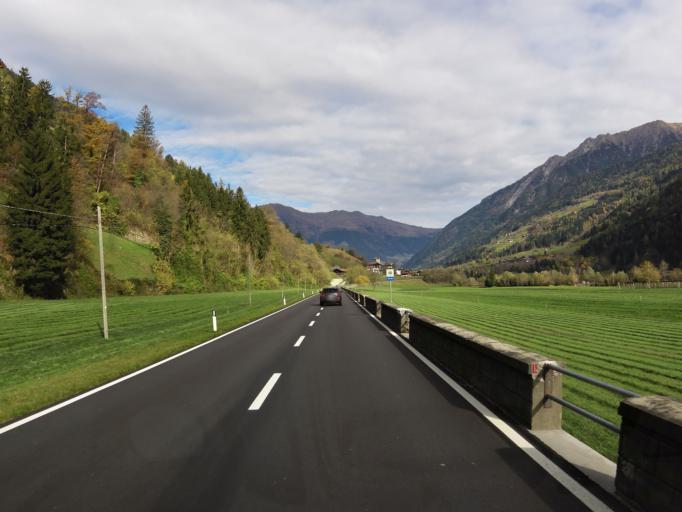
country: IT
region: Trentino-Alto Adige
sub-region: Bolzano
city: San Martino in Passiria
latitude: 46.7601
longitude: 11.2085
